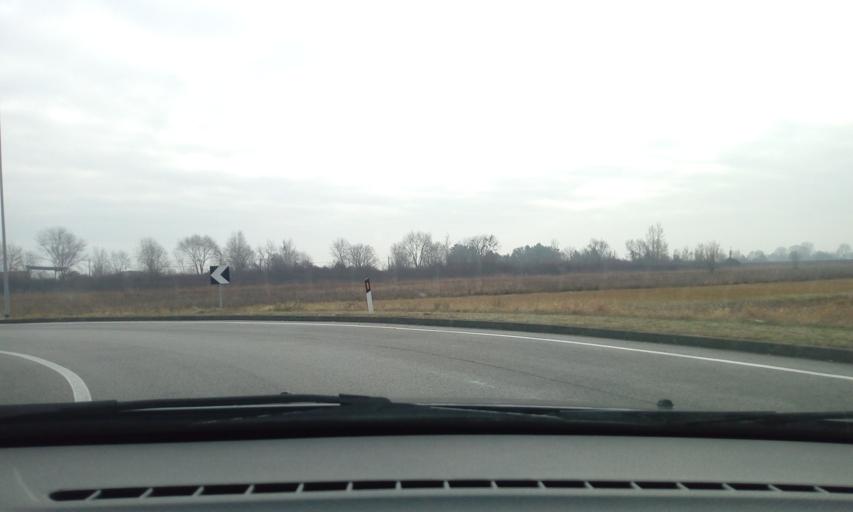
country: IT
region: Friuli Venezia Giulia
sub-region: Provincia di Gorizia
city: Mossa
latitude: 45.9282
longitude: 13.5464
